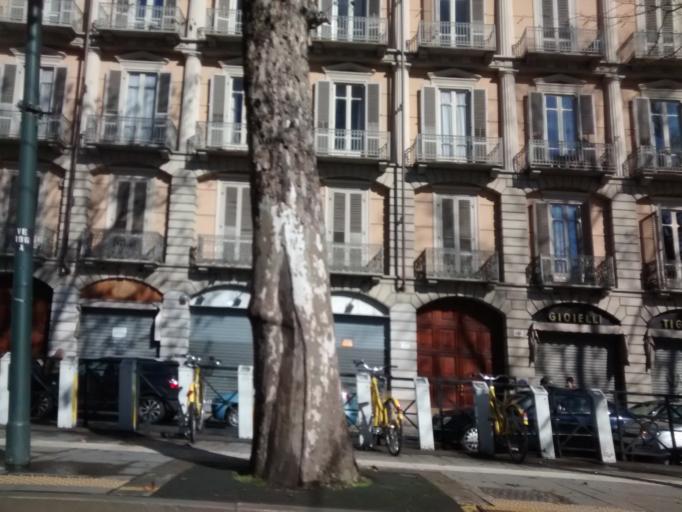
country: IT
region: Piedmont
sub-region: Provincia di Torino
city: Turin
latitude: 45.0675
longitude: 7.6658
